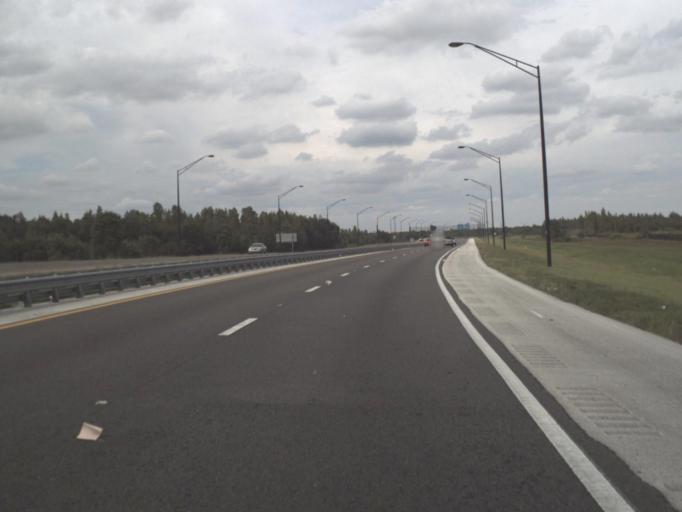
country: US
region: Florida
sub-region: Polk County
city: Winston
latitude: 28.0142
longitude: -82.0325
